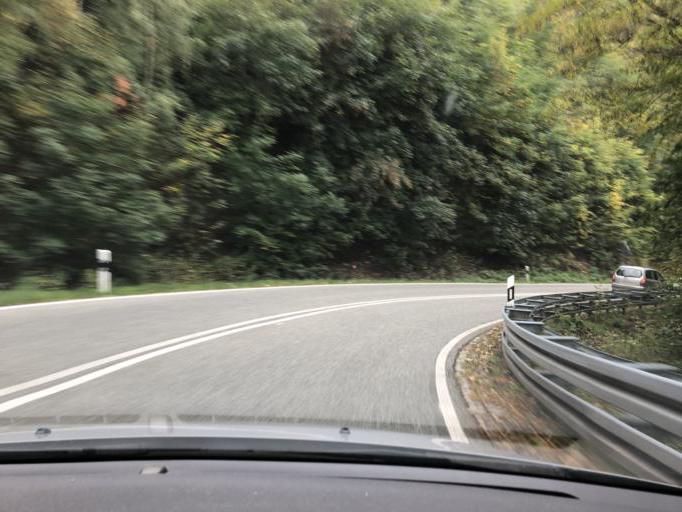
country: DE
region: Saxony-Anhalt
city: Kelbra
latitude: 51.4161
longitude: 11.0682
